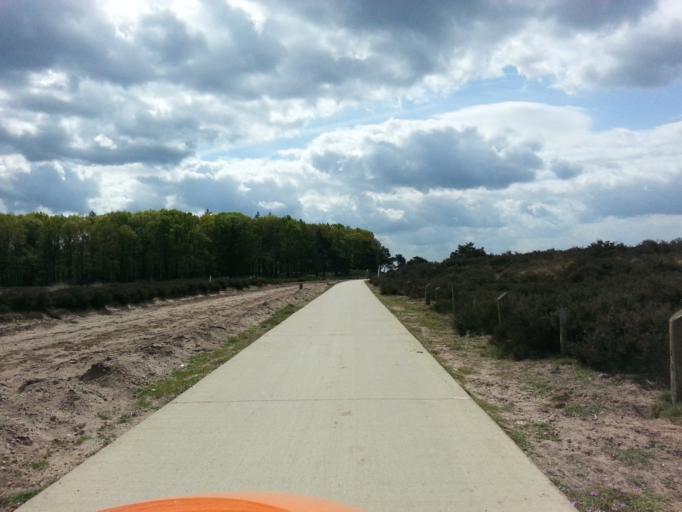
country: NL
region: Gelderland
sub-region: Gemeente Ede
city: Ede
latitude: 52.0527
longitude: 5.7056
